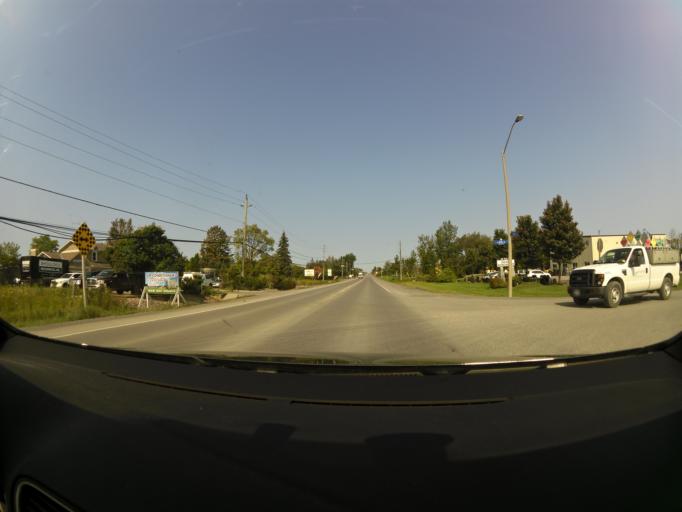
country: CA
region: Ontario
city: Bells Corners
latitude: 45.3027
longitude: -75.9837
